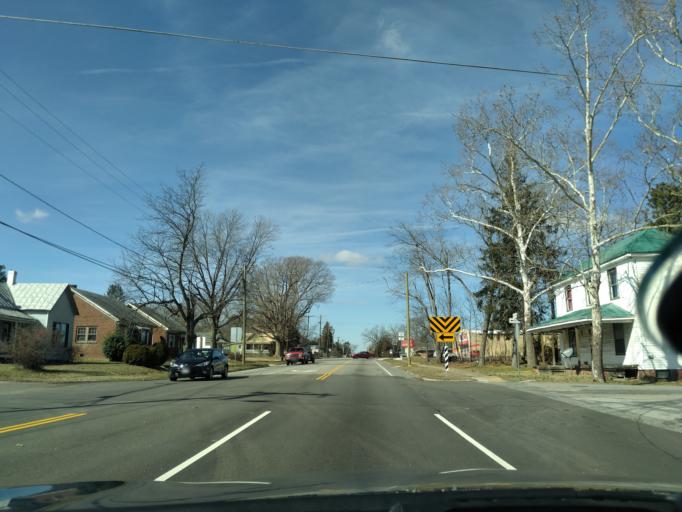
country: US
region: Virginia
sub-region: Nottoway County
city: Crewe
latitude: 37.1679
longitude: -78.1176
